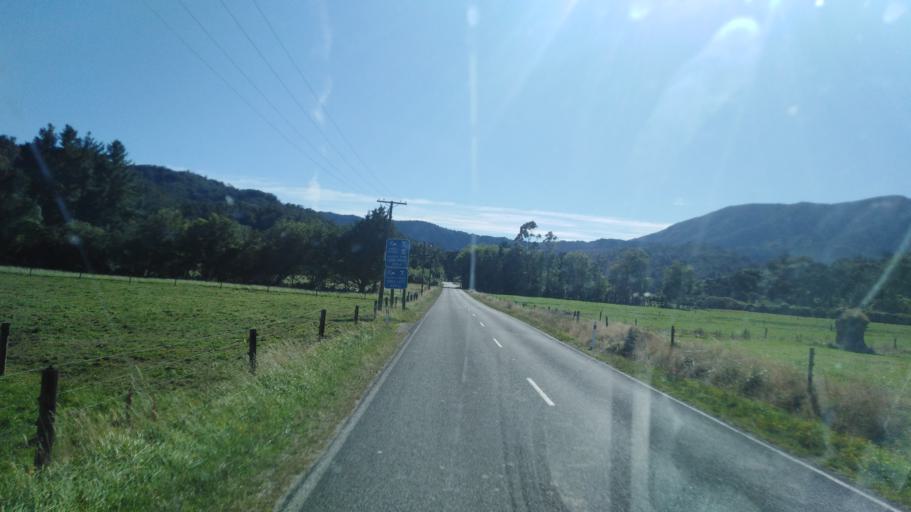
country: NZ
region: West Coast
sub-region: Buller District
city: Westport
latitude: -41.5321
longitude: 171.9628
